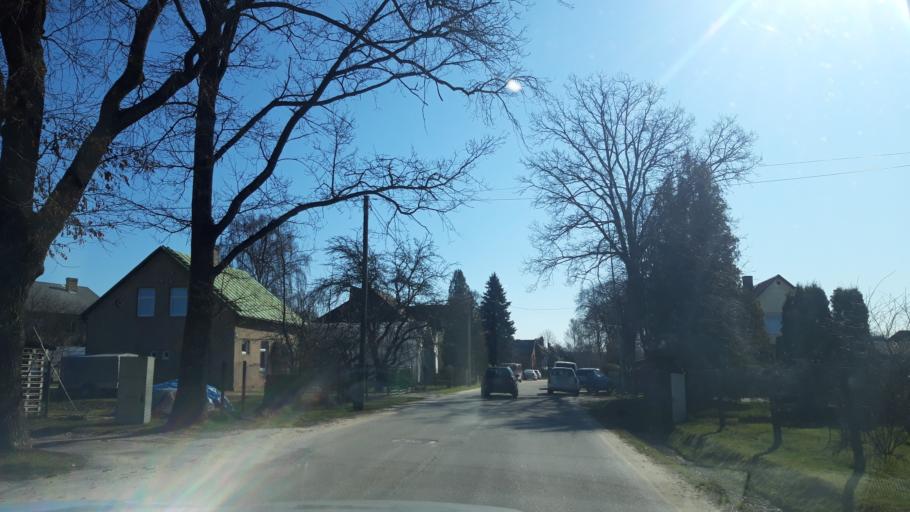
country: LV
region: Valmieras Rajons
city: Valmiera
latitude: 57.5475
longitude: 25.4523
